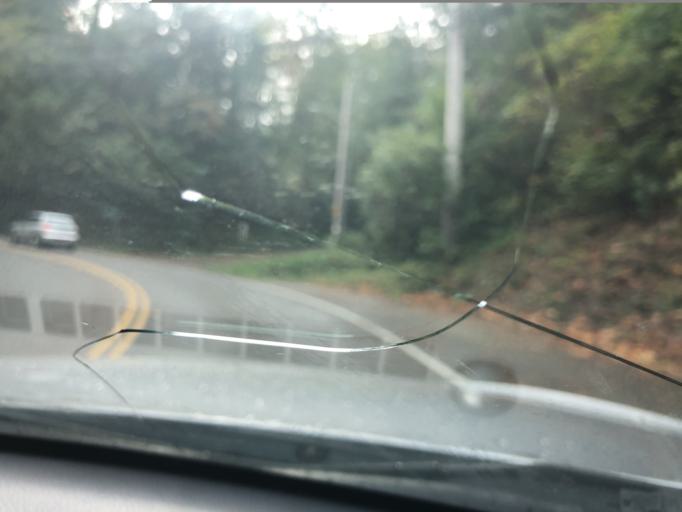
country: US
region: Washington
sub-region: King County
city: Riverbend
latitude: 47.4631
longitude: -121.7588
